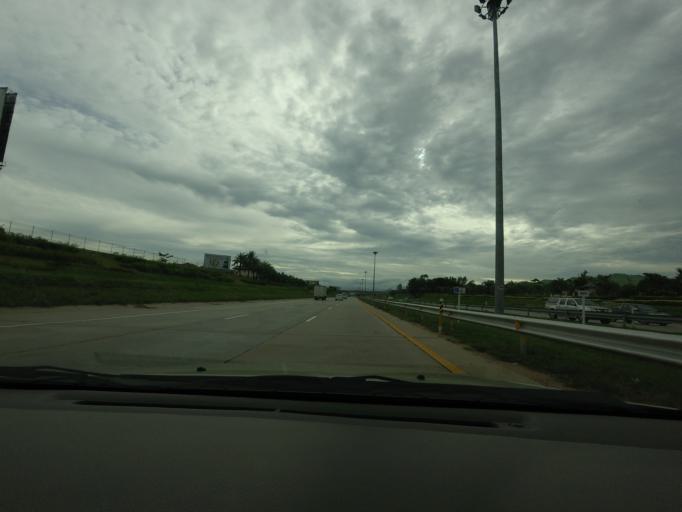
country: TH
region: Chon Buri
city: Phatthaya
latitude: 12.9510
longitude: 100.9547
